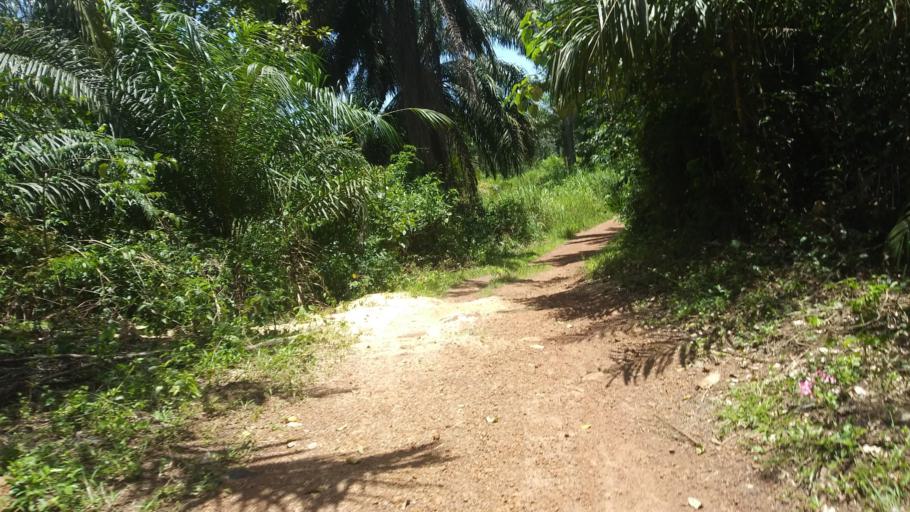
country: SL
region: Northern Province
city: Makeni
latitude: 8.9005
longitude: -11.9930
